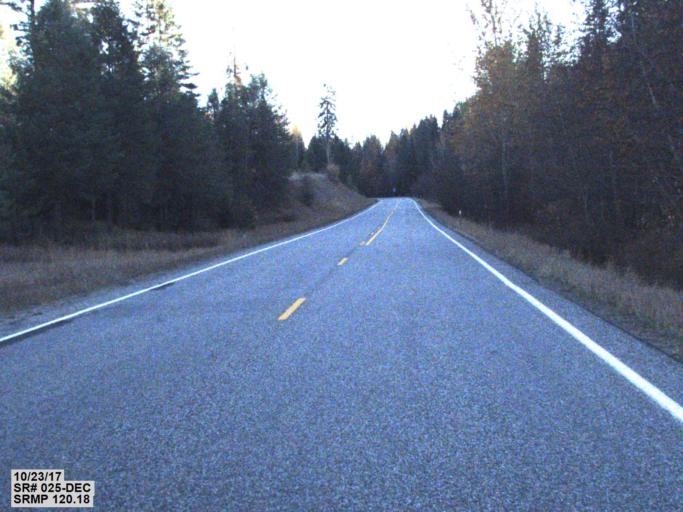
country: CA
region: British Columbia
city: Rossland
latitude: 48.9860
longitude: -117.8271
